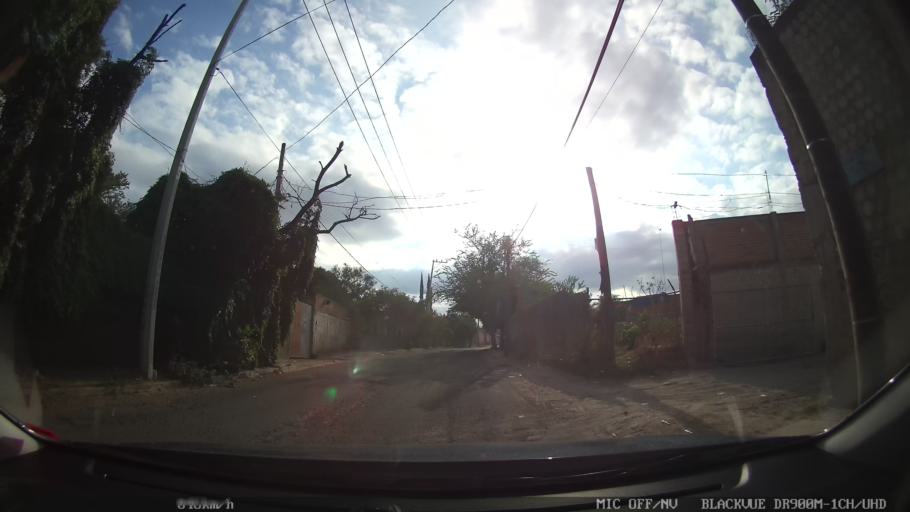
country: MX
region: Jalisco
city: Tonala
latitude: 20.6782
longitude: -103.2510
